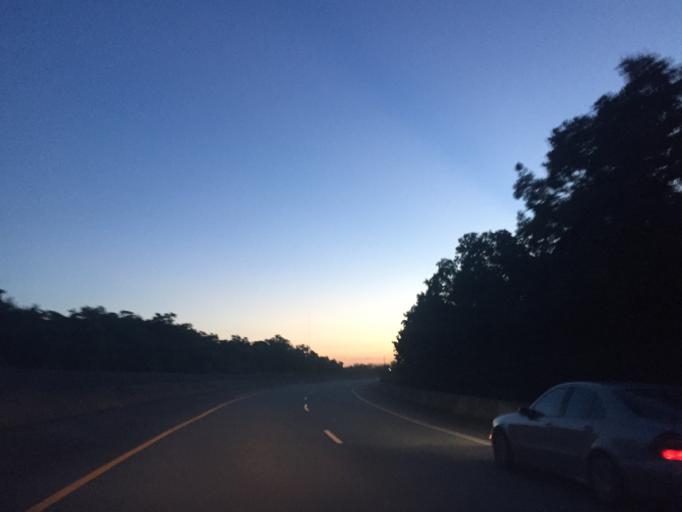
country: US
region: Georgia
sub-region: Chatham County
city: Savannah
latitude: 32.0679
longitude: -81.0761
